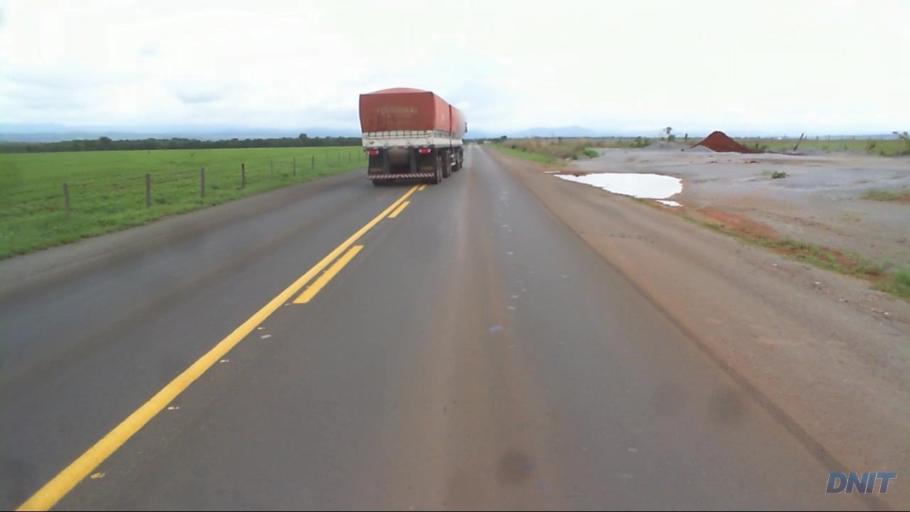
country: BR
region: Goias
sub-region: Padre Bernardo
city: Padre Bernardo
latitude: -15.1714
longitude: -48.3674
